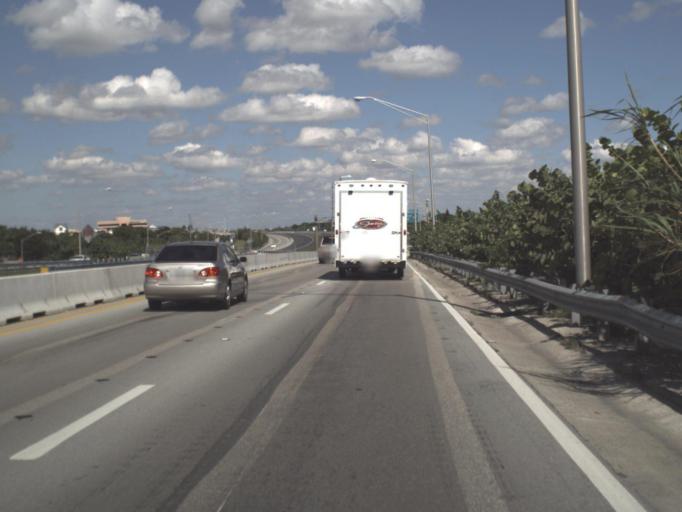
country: US
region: Florida
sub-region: Miami-Dade County
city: Goulds
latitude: 25.5673
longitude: -80.3628
